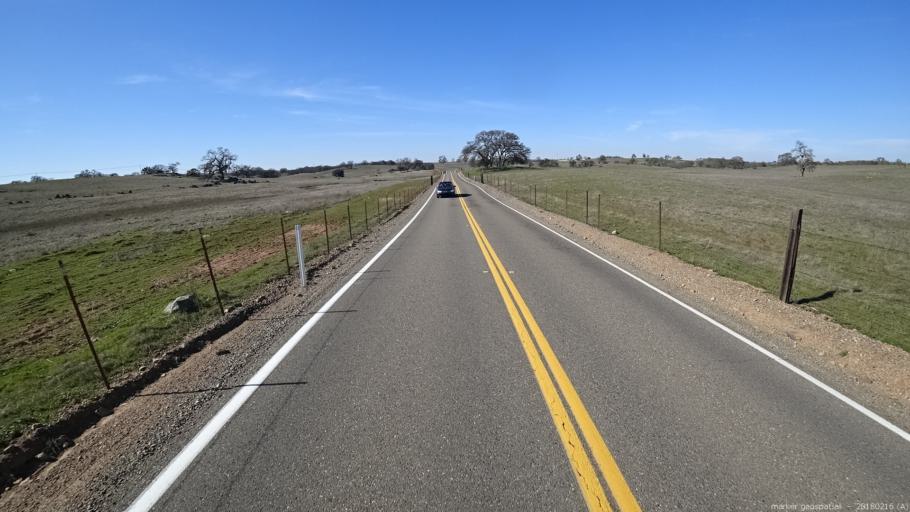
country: US
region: California
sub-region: Sacramento County
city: Rancho Murieta
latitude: 38.5596
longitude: -121.1224
